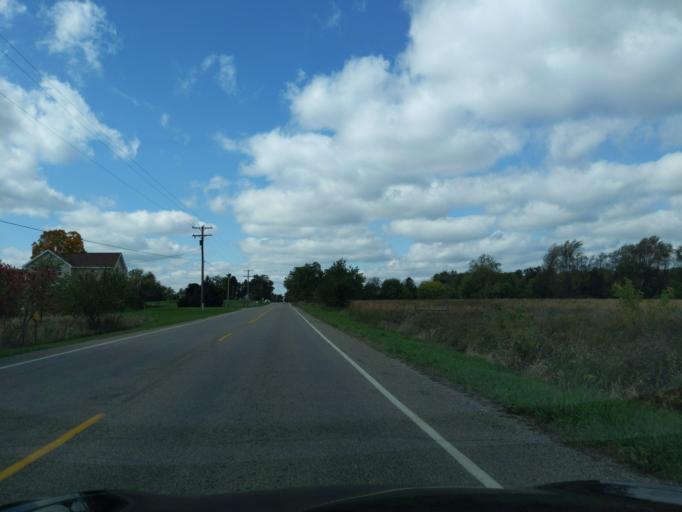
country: US
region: Michigan
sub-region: Eaton County
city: Potterville
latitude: 42.5676
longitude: -84.7394
